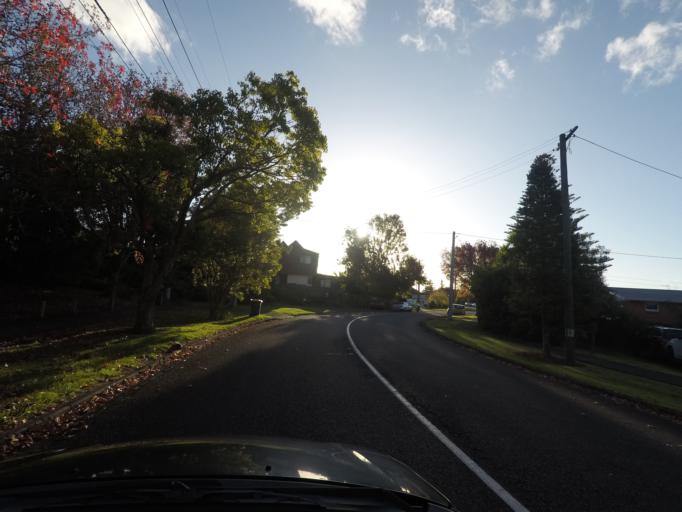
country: NZ
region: Auckland
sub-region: Auckland
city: Waitakere
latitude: -36.9024
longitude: 174.6747
